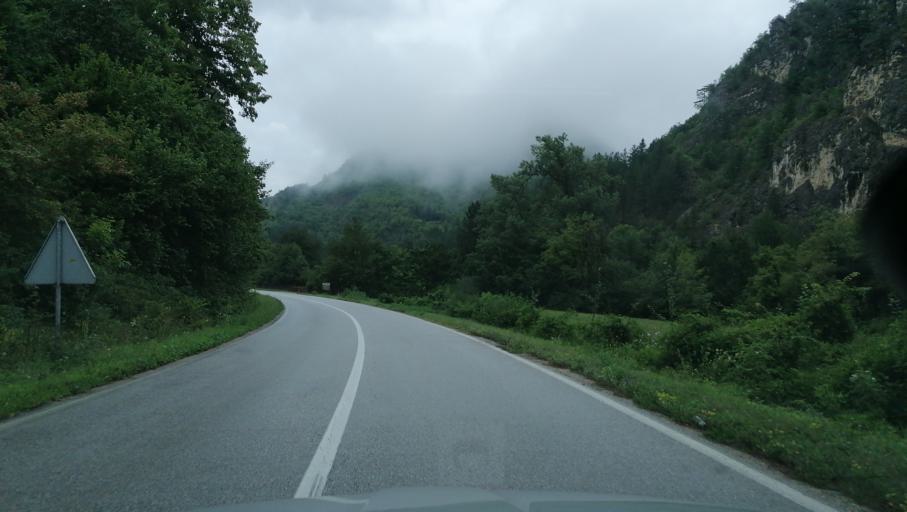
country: RS
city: Durici
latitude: 43.7531
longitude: 19.4000
